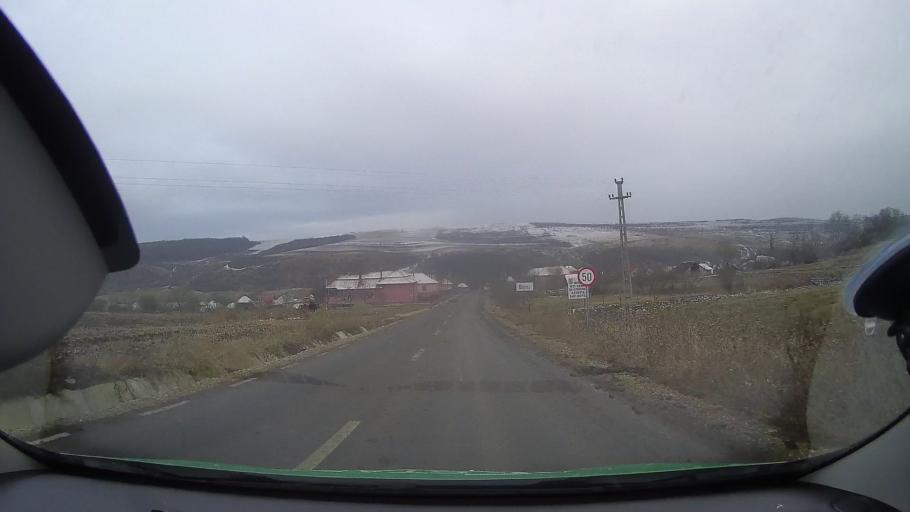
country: RO
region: Alba
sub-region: Comuna Farau
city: Farau
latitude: 46.3890
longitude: 24.0217
